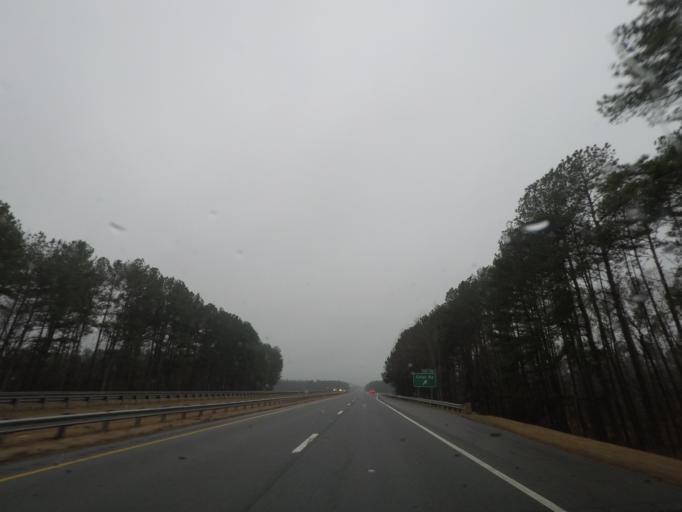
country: US
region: North Carolina
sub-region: Chatham County
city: Farmville
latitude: 35.5652
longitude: -79.1501
